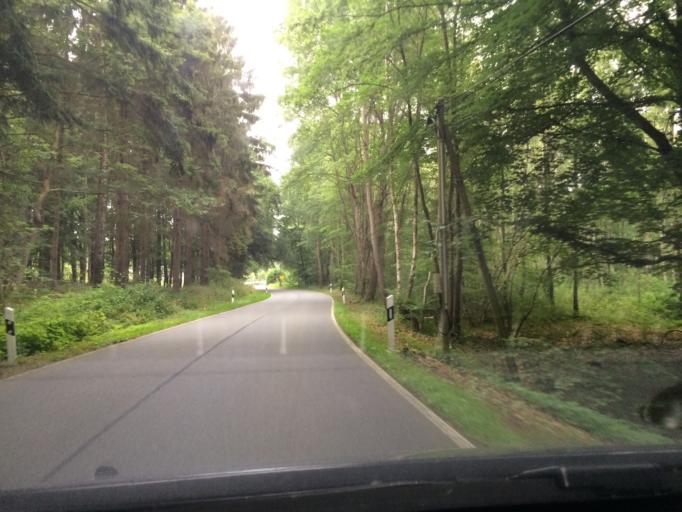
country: DE
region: Mecklenburg-Vorpommern
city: Prohn
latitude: 54.4293
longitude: 13.0265
